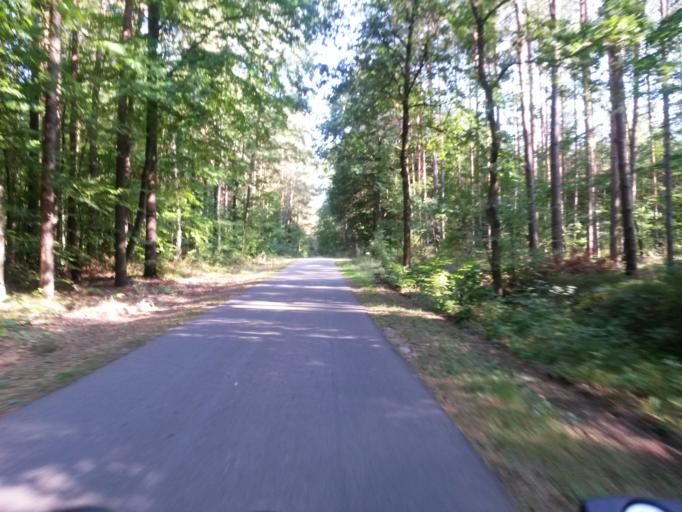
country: DE
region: Brandenburg
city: Templin
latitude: 53.1565
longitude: 13.4370
